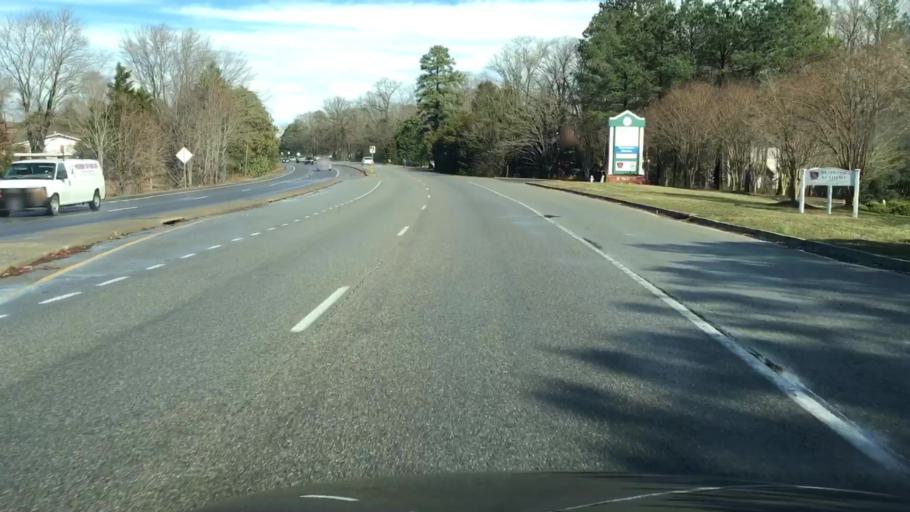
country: US
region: Virginia
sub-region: Chesterfield County
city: Bon Air
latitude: 37.5257
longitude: -77.6012
